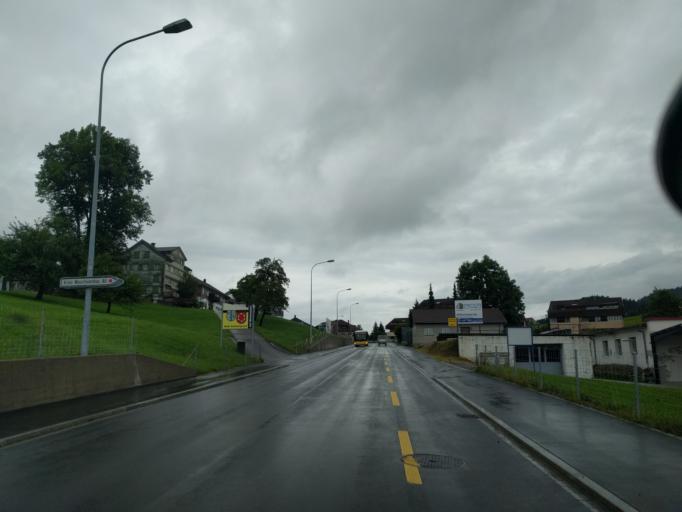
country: CH
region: Appenzell Ausserrhoden
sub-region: Bezirk Hinterland
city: Schwellbrunn
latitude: 47.3306
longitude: 9.2300
